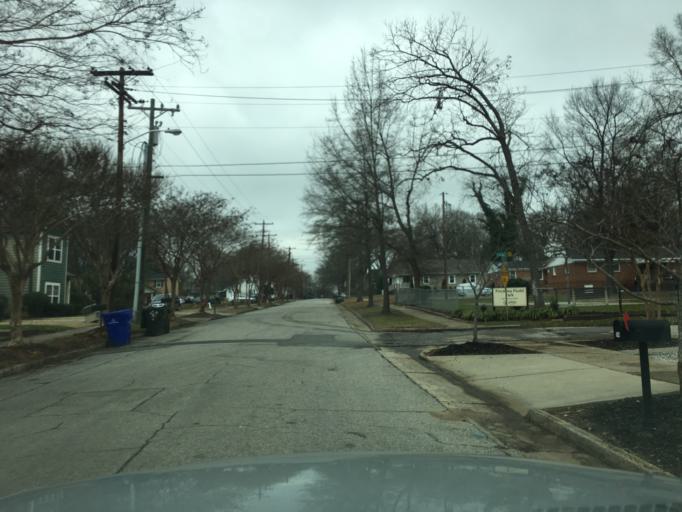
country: US
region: South Carolina
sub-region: Greenville County
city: Greenville
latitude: 34.8606
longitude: -82.4094
